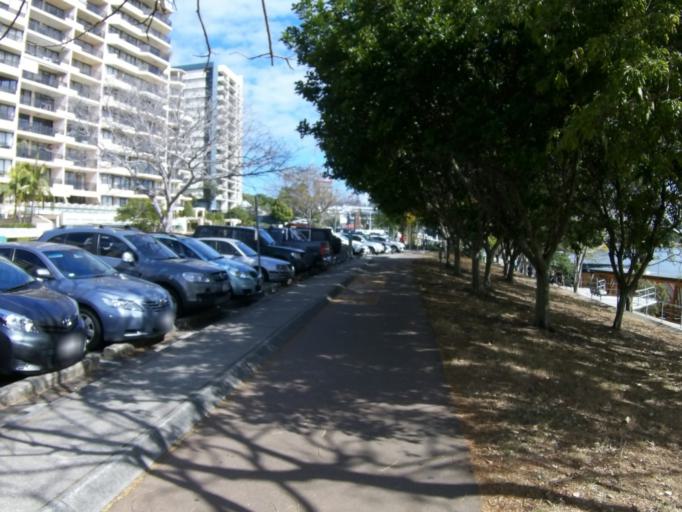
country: AU
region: Queensland
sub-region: Brisbane
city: South Brisbane
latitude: -27.4822
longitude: 153.0292
